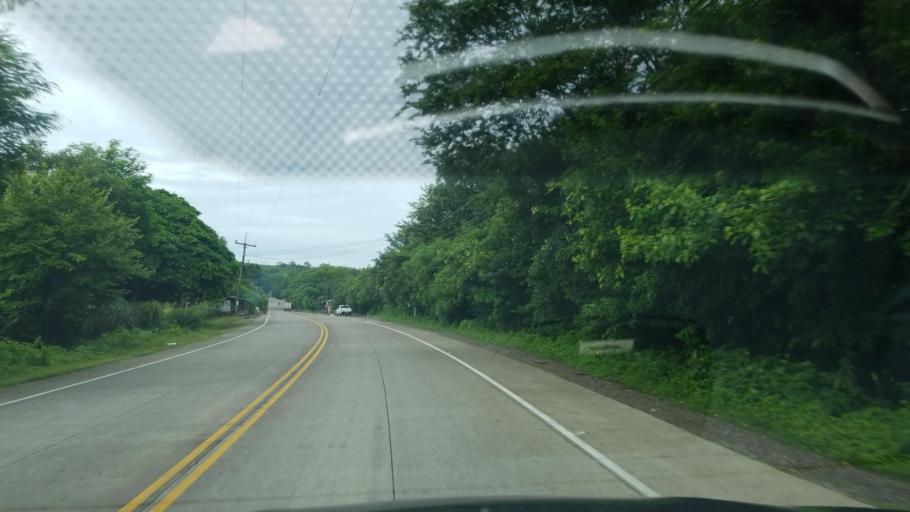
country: HN
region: Choluteca
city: Pespire
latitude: 13.6578
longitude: -87.3645
